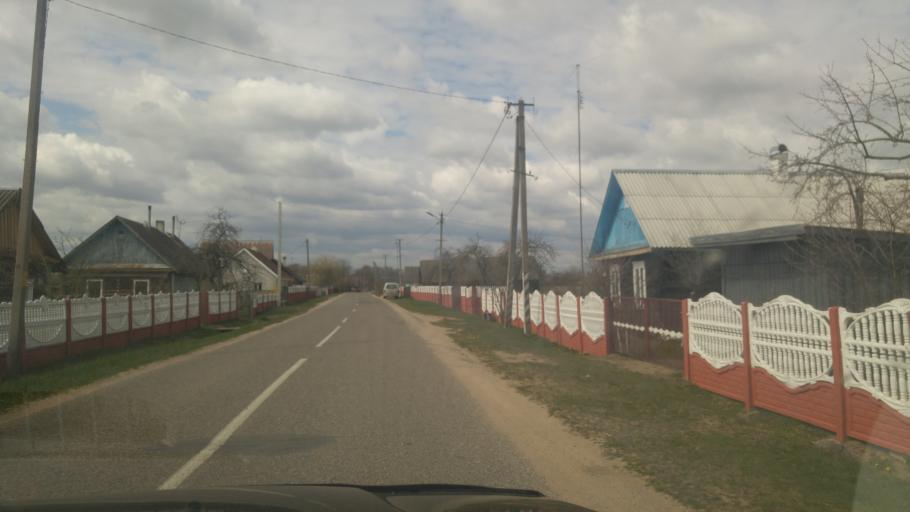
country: BY
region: Minsk
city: Pukhavichy
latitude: 53.4162
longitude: 28.2682
